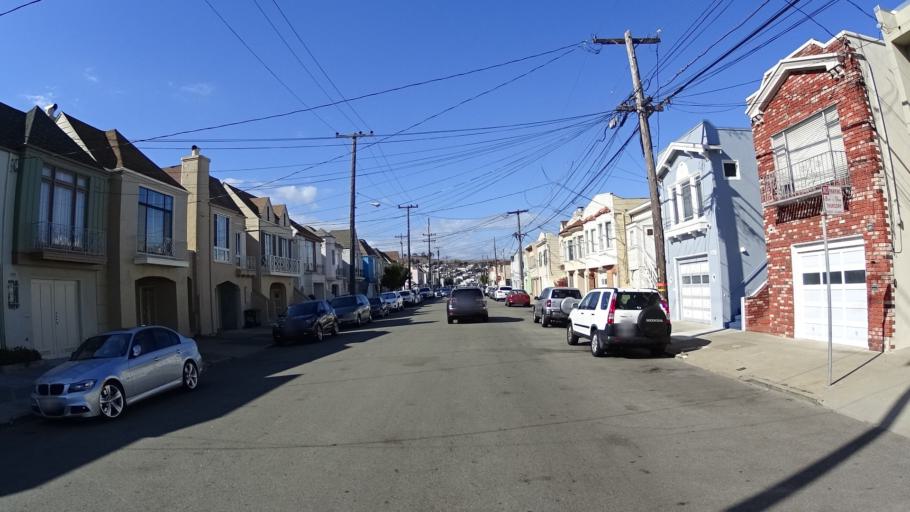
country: US
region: California
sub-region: San Mateo County
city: Brisbane
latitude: 37.7283
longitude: -122.4071
